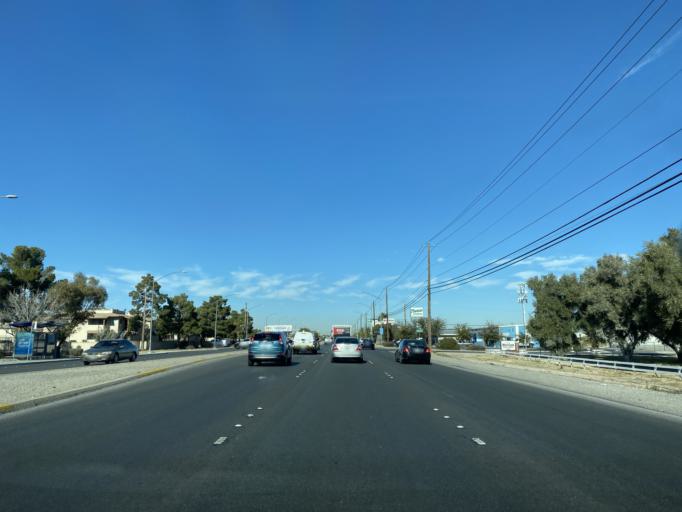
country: US
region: Nevada
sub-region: Clark County
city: Las Vegas
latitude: 36.2269
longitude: -115.2208
